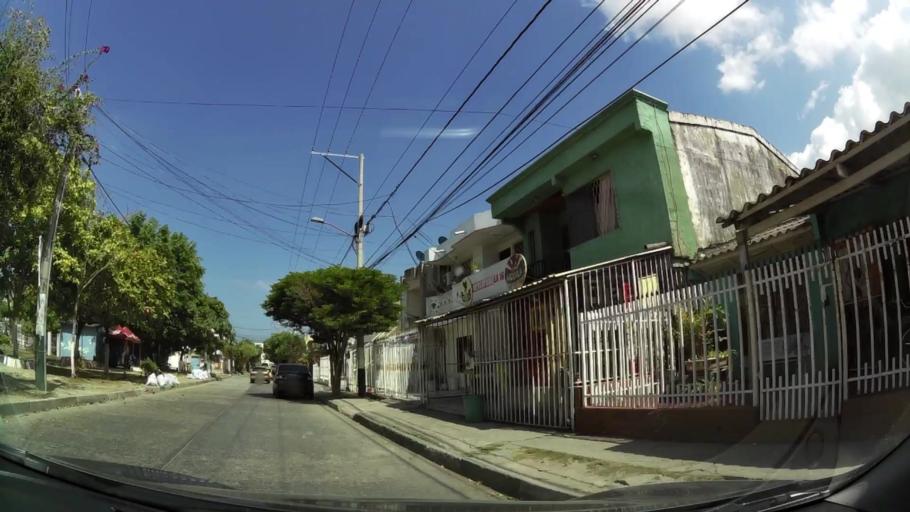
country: CO
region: Bolivar
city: Cartagena
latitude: 10.3785
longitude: -75.4652
